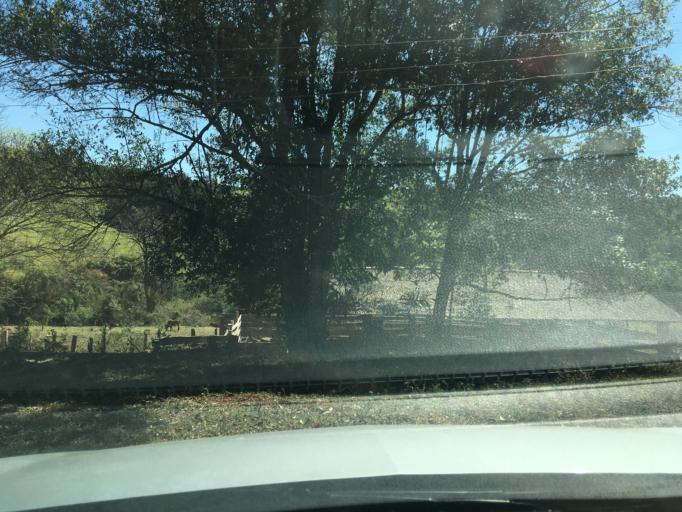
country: BR
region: Minas Gerais
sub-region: Campestre
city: Campestre
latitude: -21.5966
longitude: -46.2087
